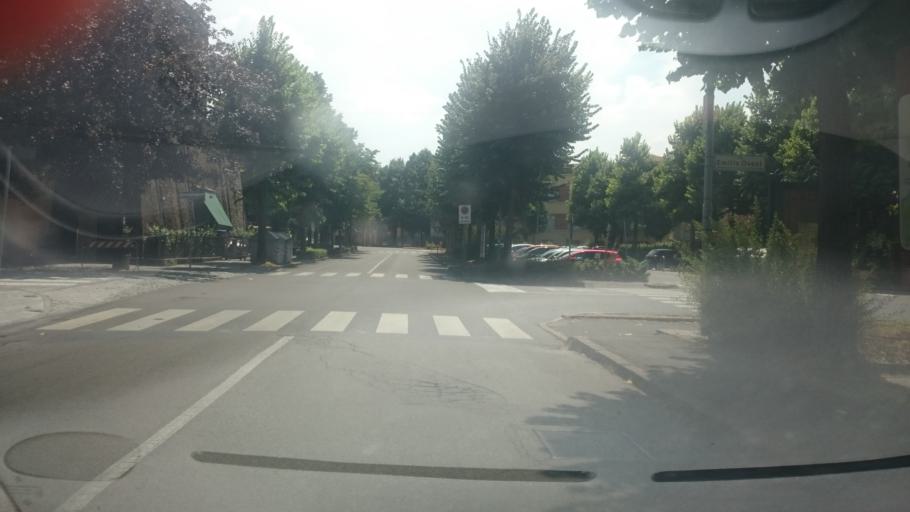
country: IT
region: Emilia-Romagna
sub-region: Provincia di Reggio Emilia
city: Rubiera
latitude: 44.6541
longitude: 10.7809
